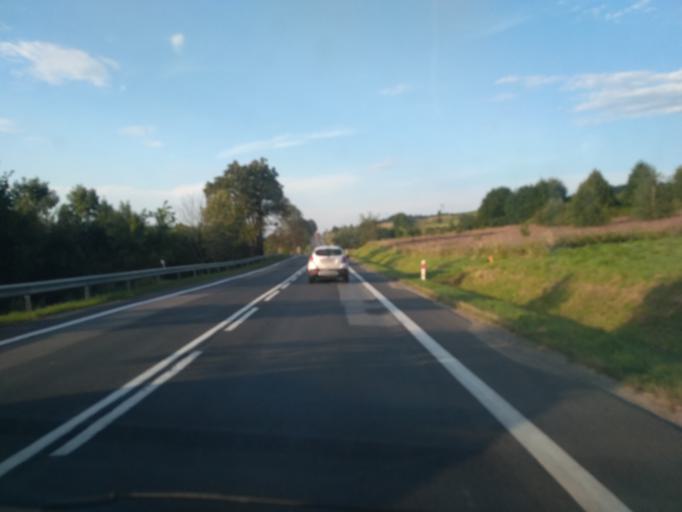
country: PL
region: Subcarpathian Voivodeship
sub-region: Powiat krosnienski
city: Dukla
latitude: 49.5992
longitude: 21.7213
